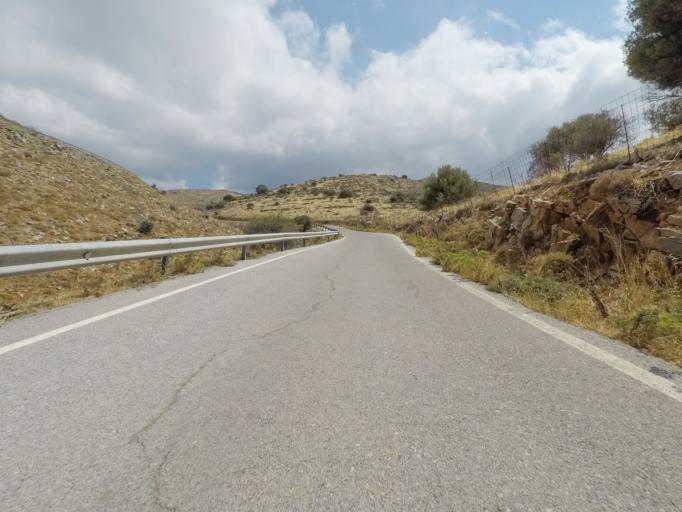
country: GR
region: Crete
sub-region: Nomos Lasithiou
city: Elounda
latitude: 35.3122
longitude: 25.6773
